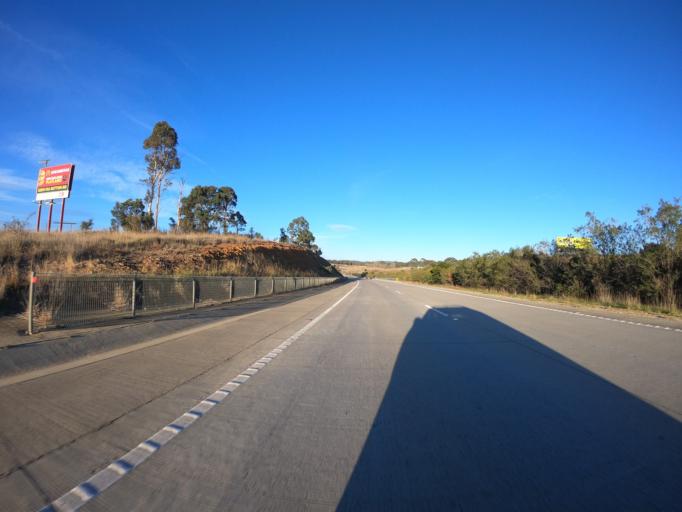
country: AU
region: New South Wales
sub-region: Yass Valley
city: Gundaroo
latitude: -35.1181
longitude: 149.3504
